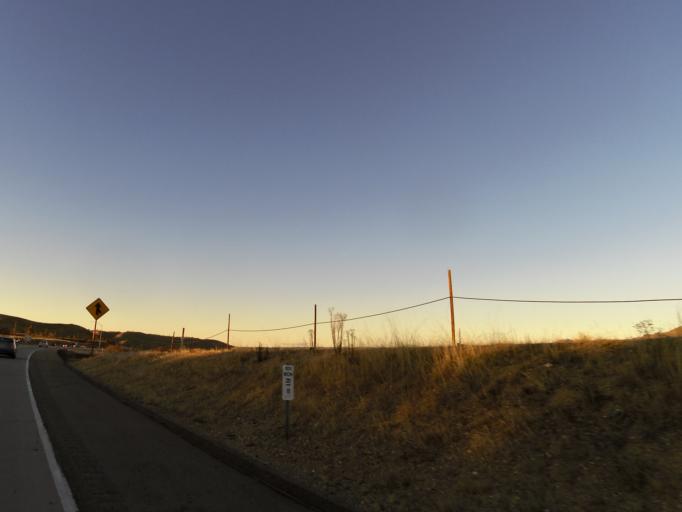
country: US
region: California
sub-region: San Luis Obispo County
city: San Miguel
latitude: 35.8006
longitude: -120.7447
